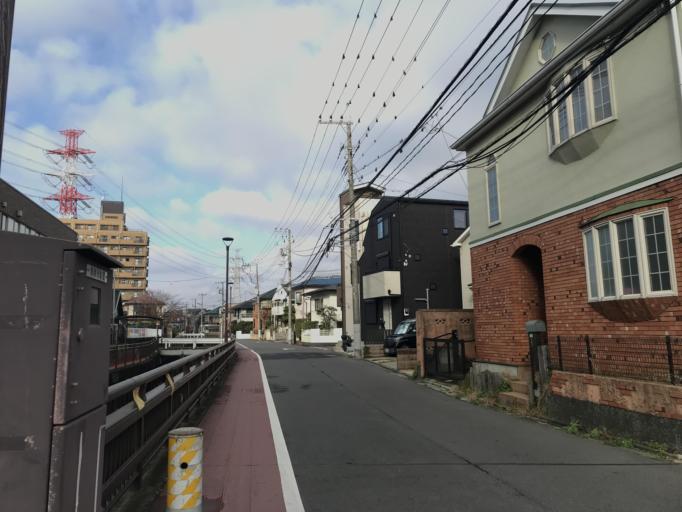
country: JP
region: Chiba
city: Funabashi
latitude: 35.7103
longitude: 139.9840
